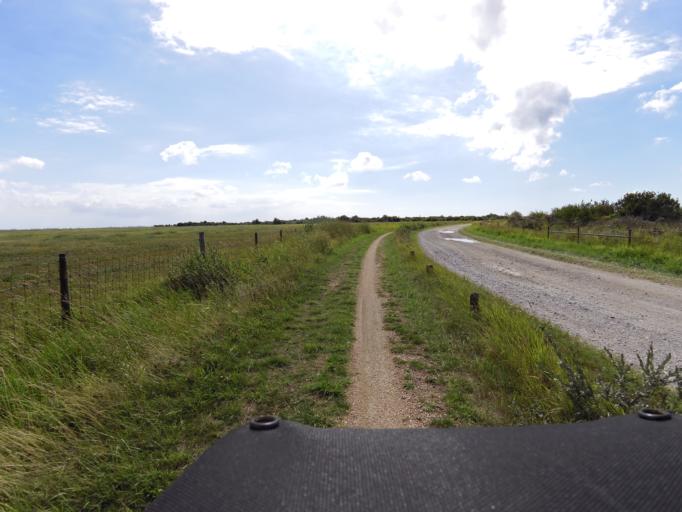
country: NL
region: South Holland
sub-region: Gemeente Goeree-Overflakkee
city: Dirksland
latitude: 51.7574
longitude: 4.0329
